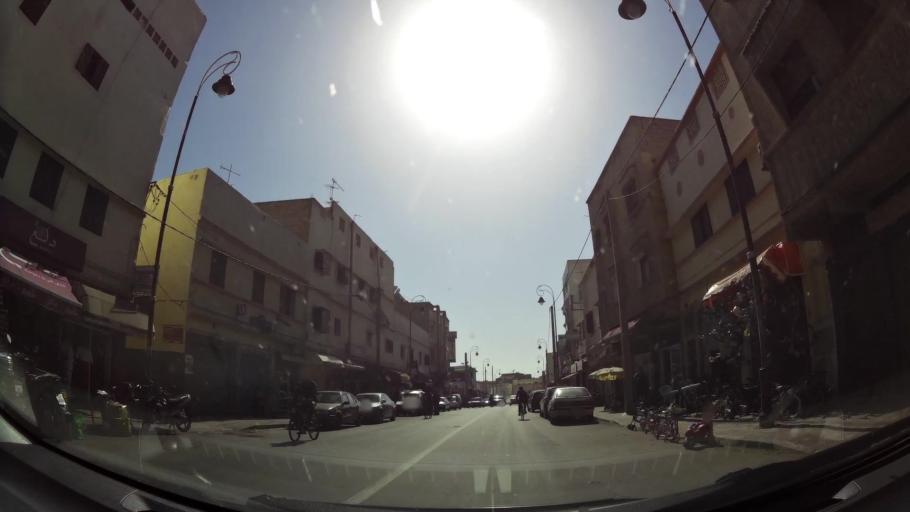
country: MA
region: Souss-Massa-Draa
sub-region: Inezgane-Ait Mellou
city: Inezgane
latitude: 30.3704
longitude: -9.5376
